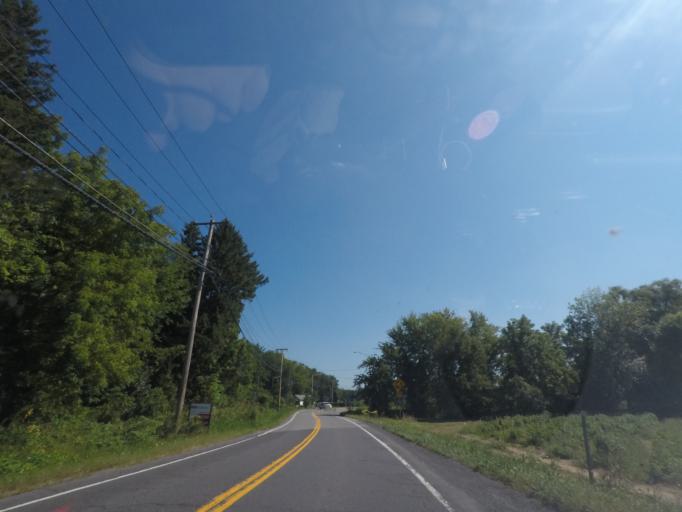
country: US
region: New York
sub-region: Albany County
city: Roessleville
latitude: 42.7399
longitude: -73.7914
